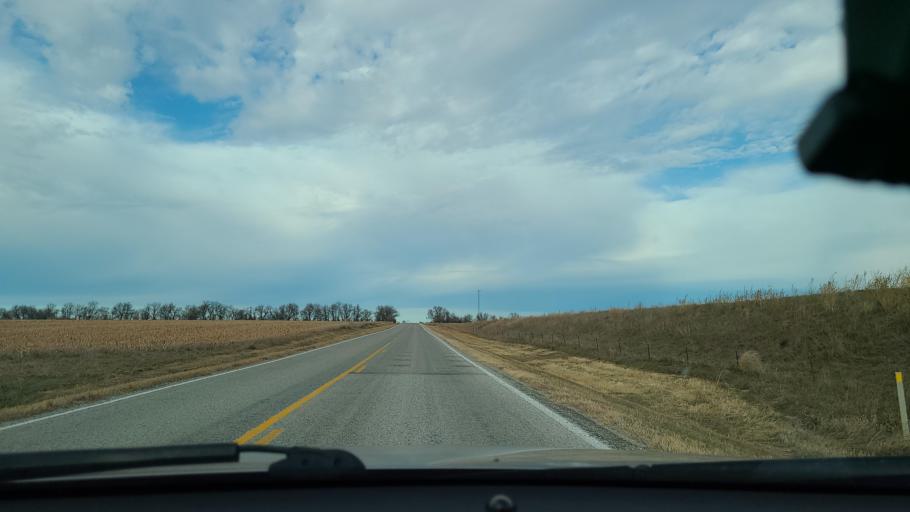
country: US
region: Kansas
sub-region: McPherson County
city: Inman
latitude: 38.3513
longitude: -97.9244
